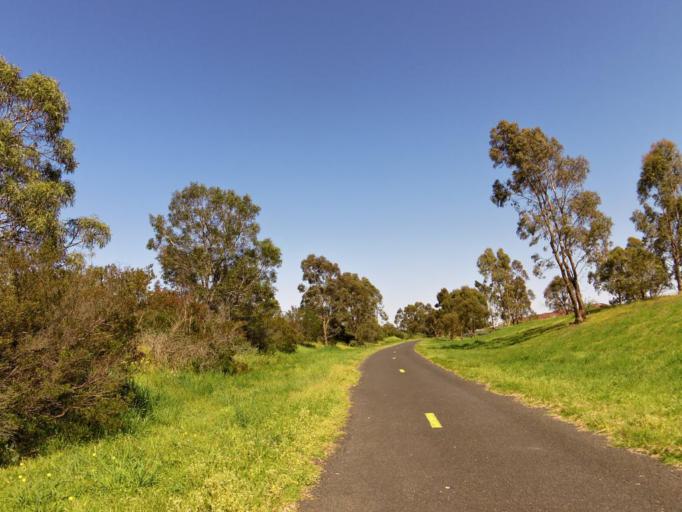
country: AU
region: Victoria
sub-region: Whittlesea
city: Thomastown
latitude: -37.6864
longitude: 145.0013
